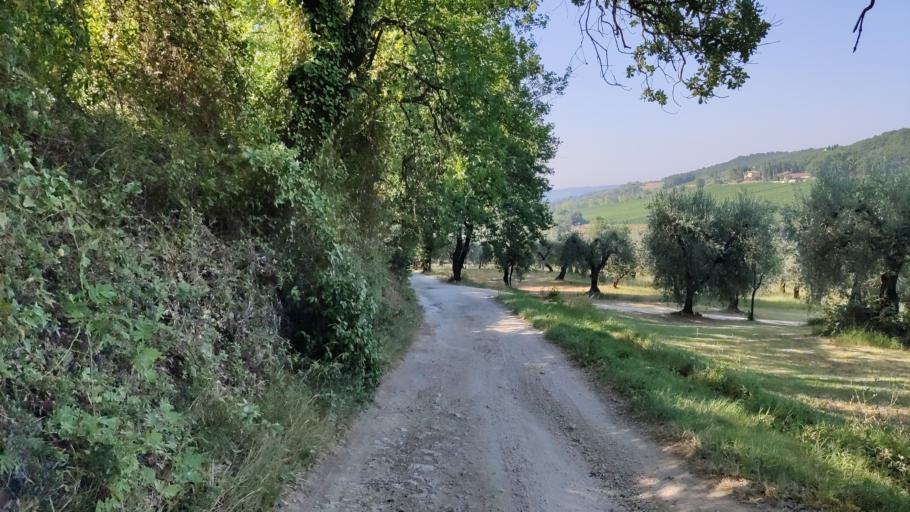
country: IT
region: Umbria
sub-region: Provincia di Terni
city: Amelia
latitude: 42.5302
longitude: 12.4102
